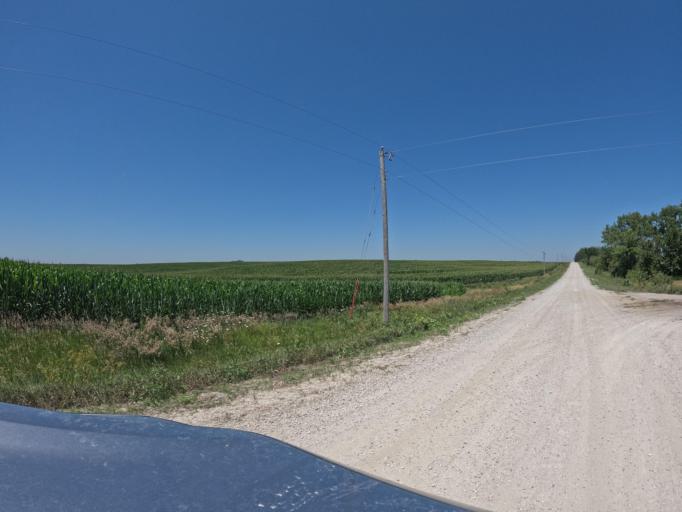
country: US
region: Iowa
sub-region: Keokuk County
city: Sigourney
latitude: 41.4569
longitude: -92.3358
